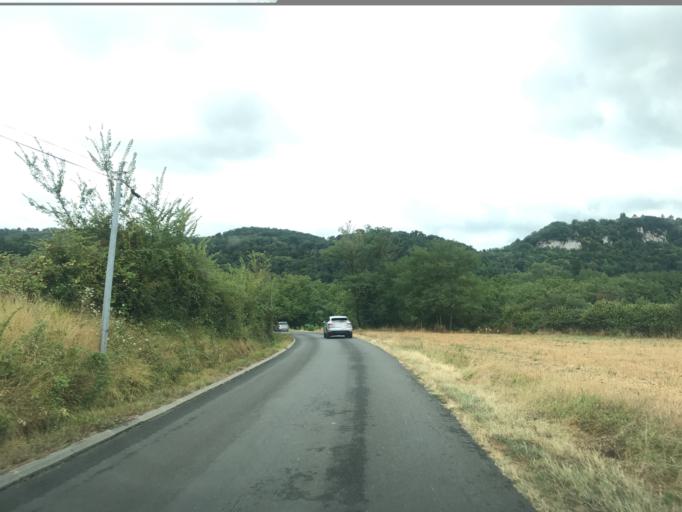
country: FR
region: Aquitaine
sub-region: Departement de la Dordogne
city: Domme
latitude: 44.8125
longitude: 1.2238
